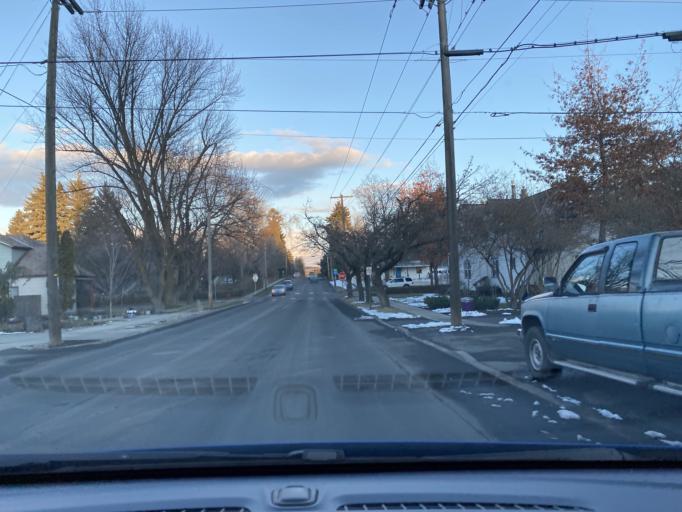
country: US
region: Idaho
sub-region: Latah County
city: Moscow
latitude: 46.7375
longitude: -116.9896
